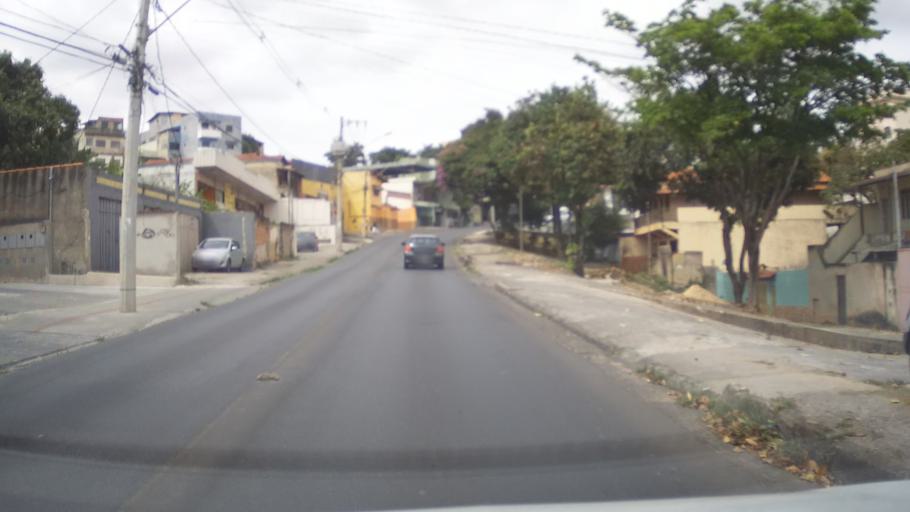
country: BR
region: Minas Gerais
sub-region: Belo Horizonte
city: Belo Horizonte
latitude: -19.8369
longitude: -43.9450
